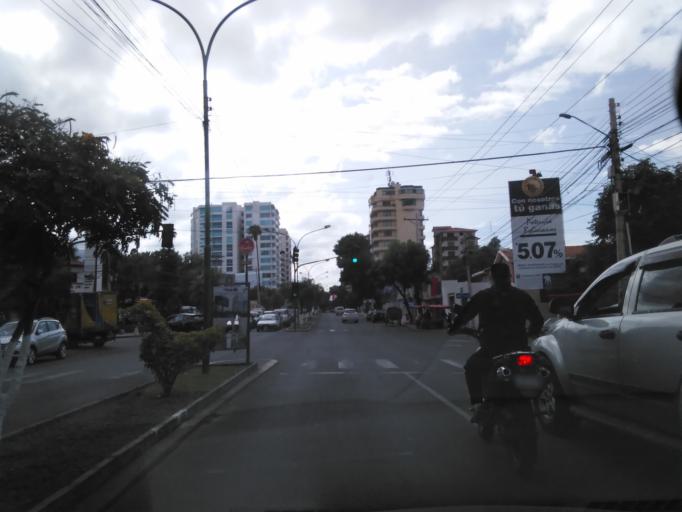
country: BO
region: Cochabamba
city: Cochabamba
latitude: -17.3726
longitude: -66.1609
